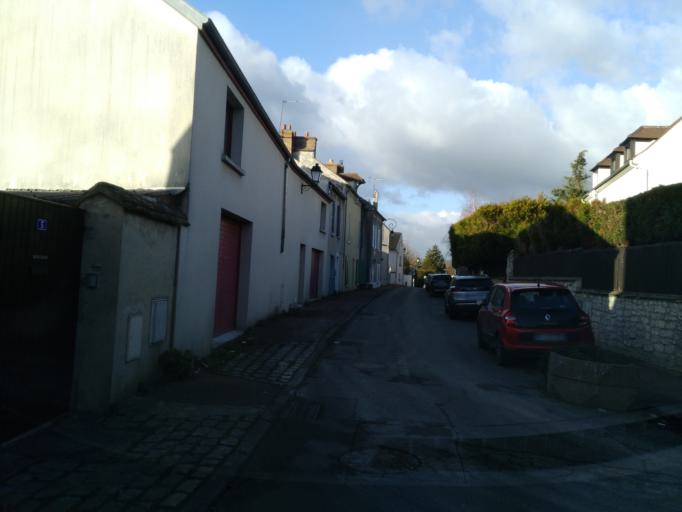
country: FR
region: Ile-de-France
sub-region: Departement des Yvelines
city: Saint-Nom-la-Breteche
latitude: 48.8576
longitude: 2.0158
